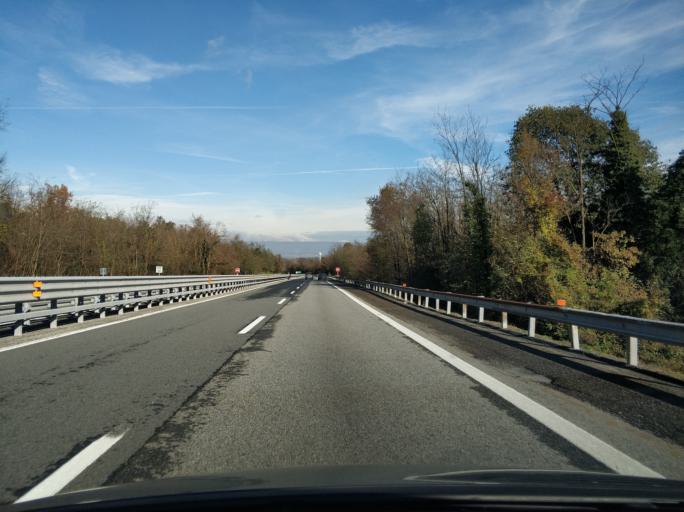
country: IT
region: Piedmont
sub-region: Provincia di Torino
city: Scarmagno
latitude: 45.3688
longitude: 7.8398
